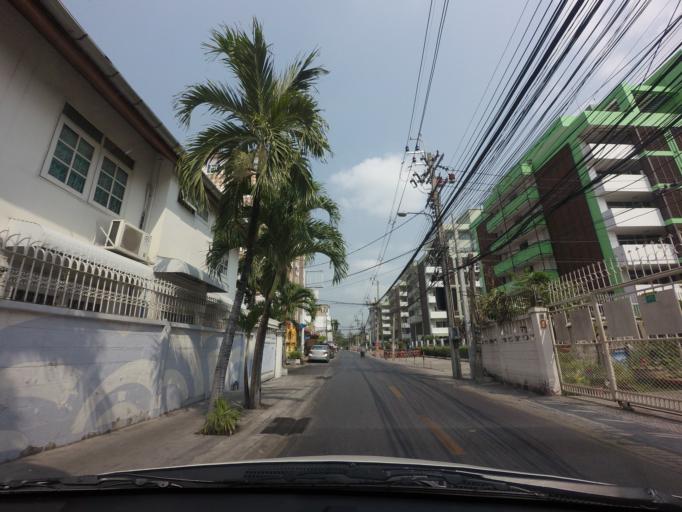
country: TH
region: Bangkok
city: Chatuchak
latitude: 13.8516
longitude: 100.5807
